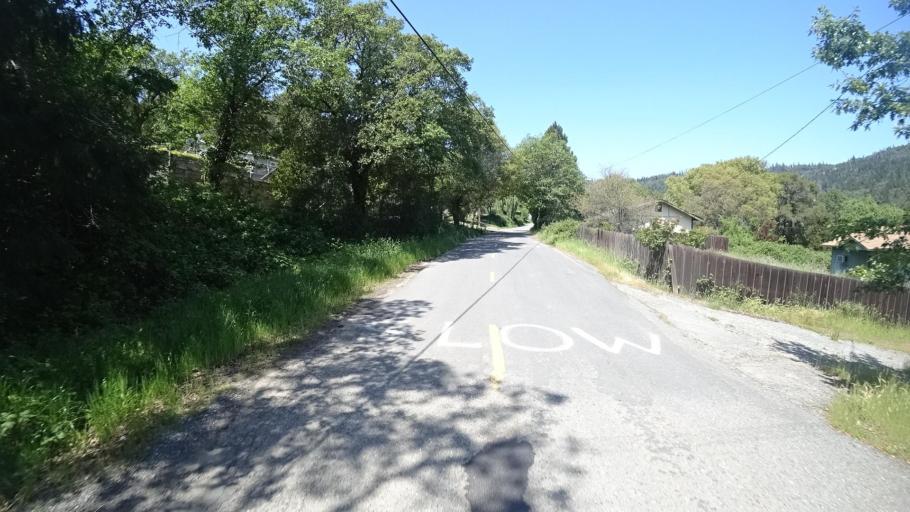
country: US
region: California
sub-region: Humboldt County
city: Redway
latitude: 40.1746
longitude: -123.6071
